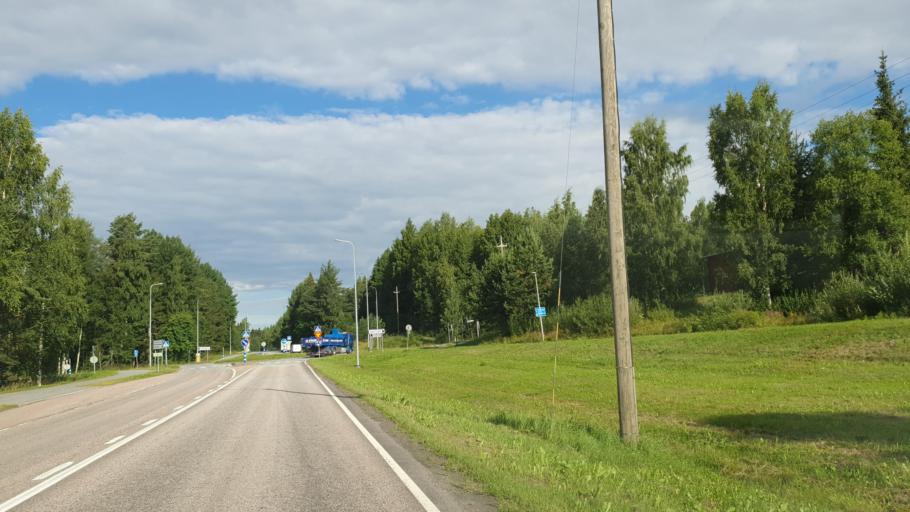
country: FI
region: Central Finland
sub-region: Jyvaeskylae
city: Saeynaetsalo
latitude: 62.1793
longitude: 25.7327
